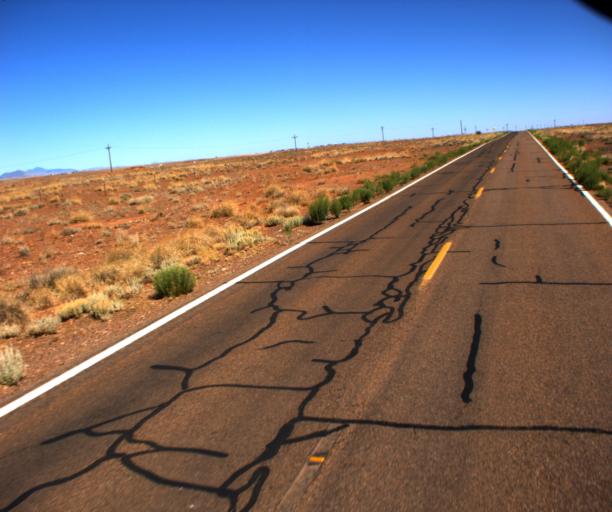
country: US
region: Arizona
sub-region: Coconino County
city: LeChee
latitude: 35.2748
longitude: -110.9781
